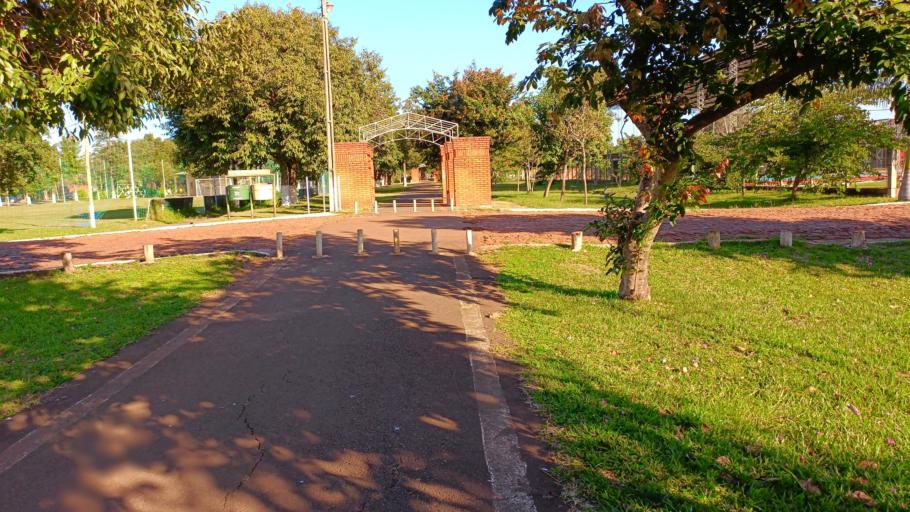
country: PY
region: Itapua
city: Carmen del Parana
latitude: -27.1569
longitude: -56.2405
